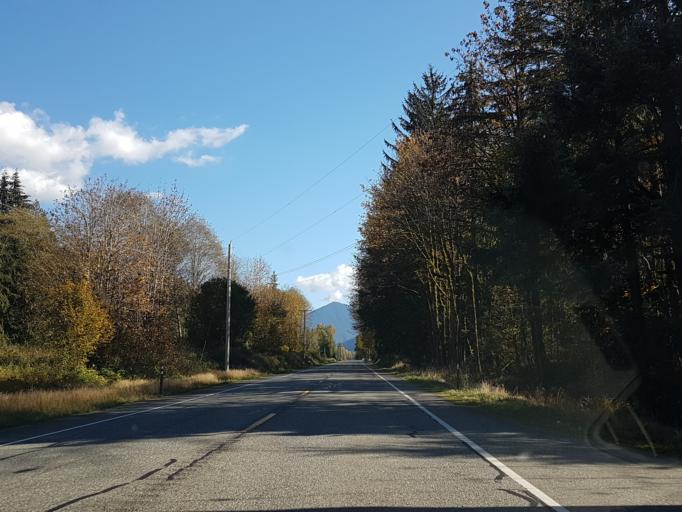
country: US
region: Washington
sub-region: Snohomish County
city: Gold Bar
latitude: 47.7774
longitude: -121.4919
